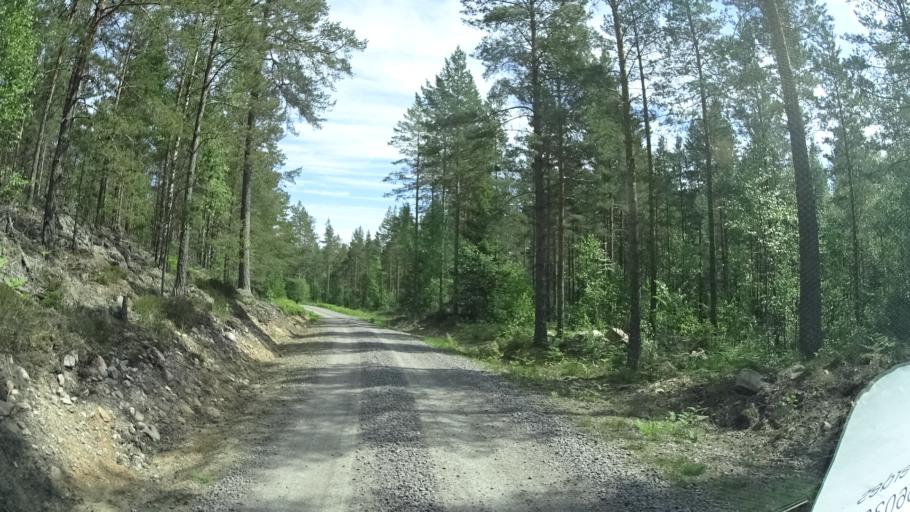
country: SE
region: OEstergoetland
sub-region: Norrkopings Kommun
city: Svartinge
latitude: 58.7707
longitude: 15.9584
